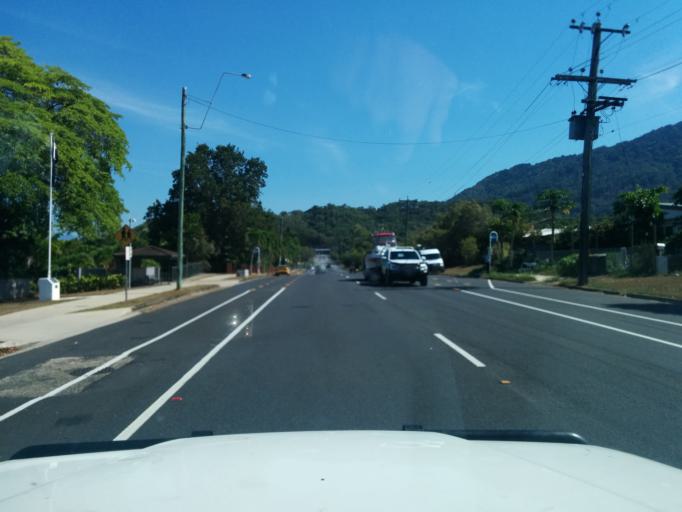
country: AU
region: Queensland
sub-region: Cairns
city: Redlynch
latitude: -16.9078
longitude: 145.7284
